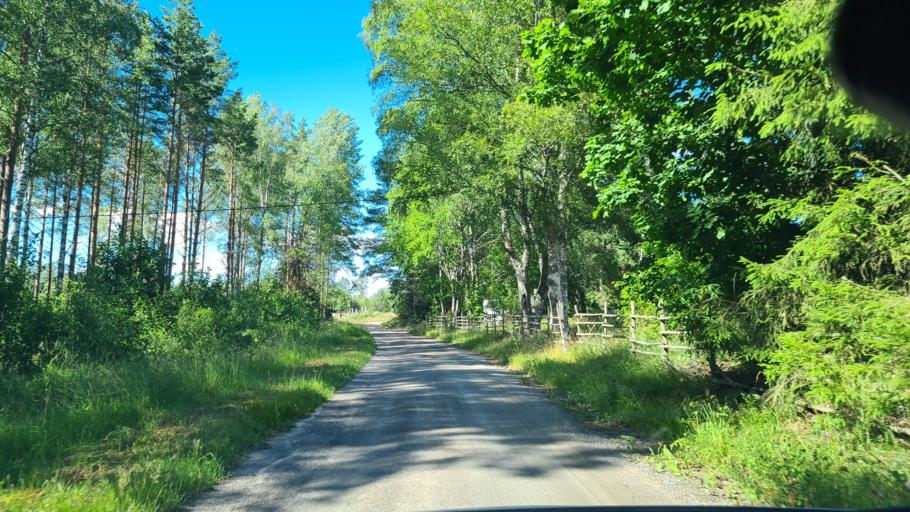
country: SE
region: OEstergoetland
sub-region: Norrkopings Kommun
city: Krokek
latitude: 58.6977
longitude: 16.4271
